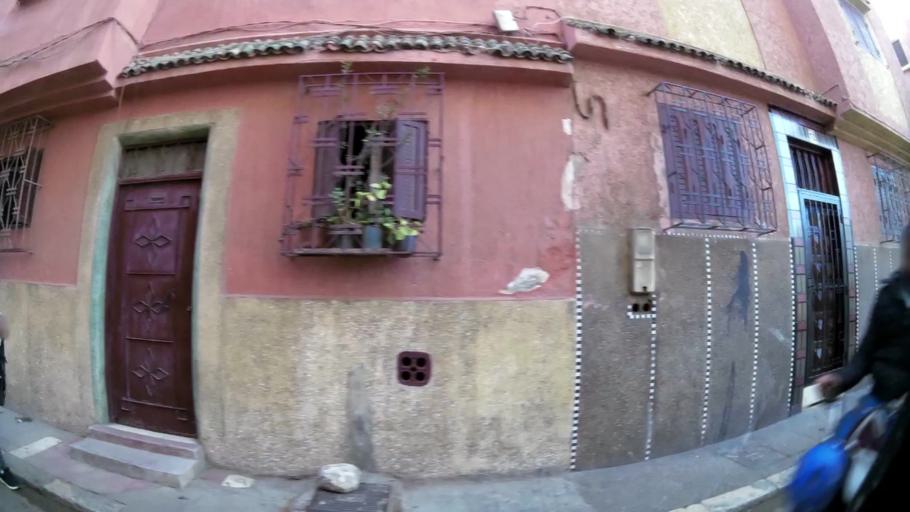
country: MA
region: Grand Casablanca
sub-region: Mohammedia
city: Mohammedia
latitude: 33.7003
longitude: -7.3836
